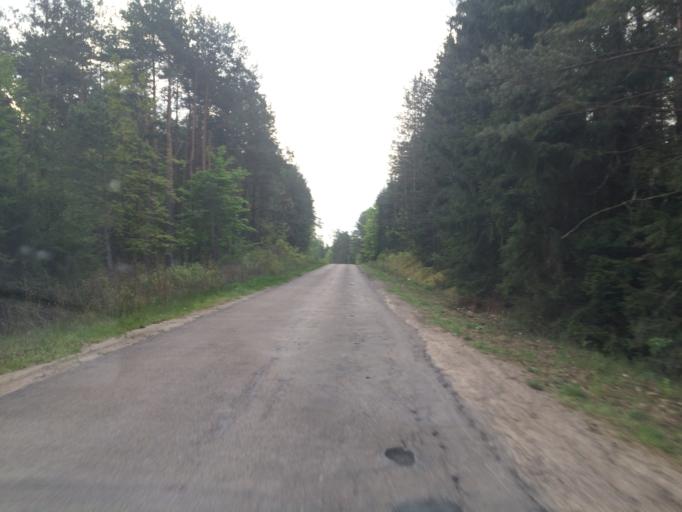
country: PL
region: Warmian-Masurian Voivodeship
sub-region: Powiat ostrodzki
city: Dabrowno
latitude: 53.3141
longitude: 20.0539
